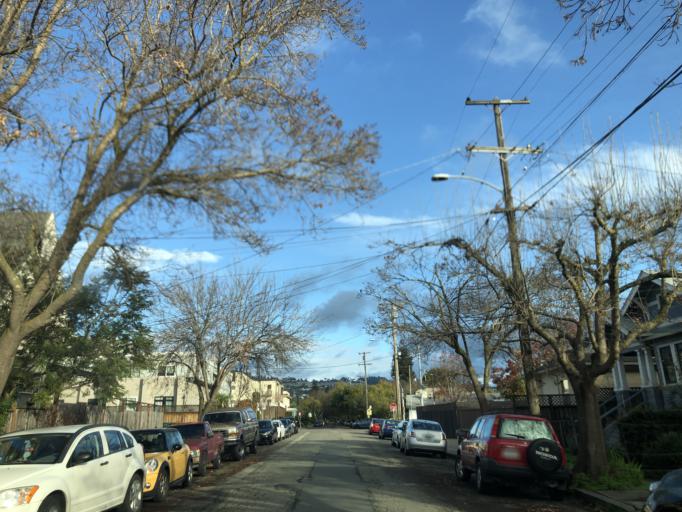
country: US
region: California
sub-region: Alameda County
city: Berkeley
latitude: 37.8486
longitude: -122.2617
